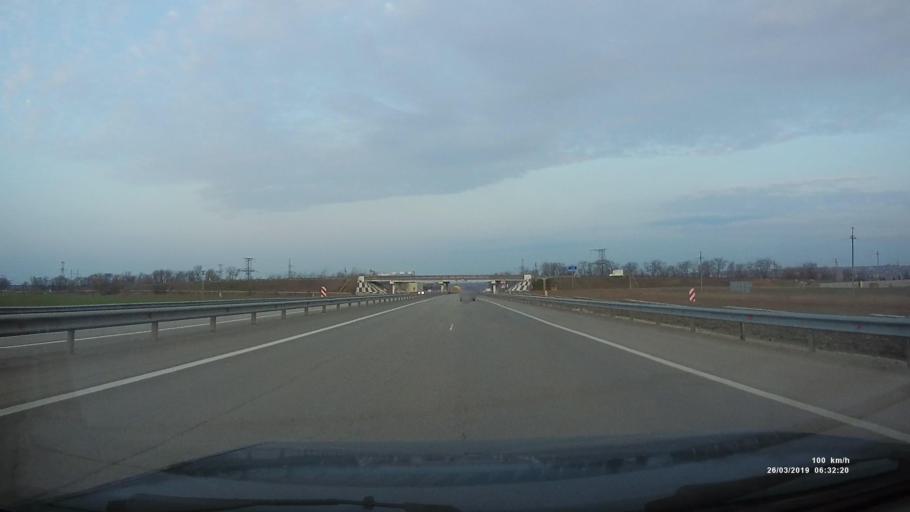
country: RU
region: Rostov
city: Kalinin
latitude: 47.2711
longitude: 39.5130
